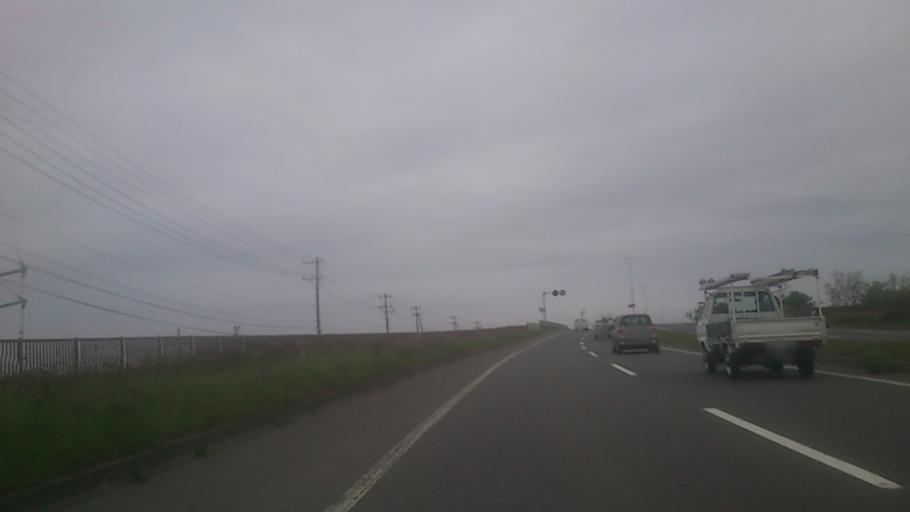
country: JP
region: Hokkaido
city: Kushiro
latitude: 42.9991
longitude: 144.4244
